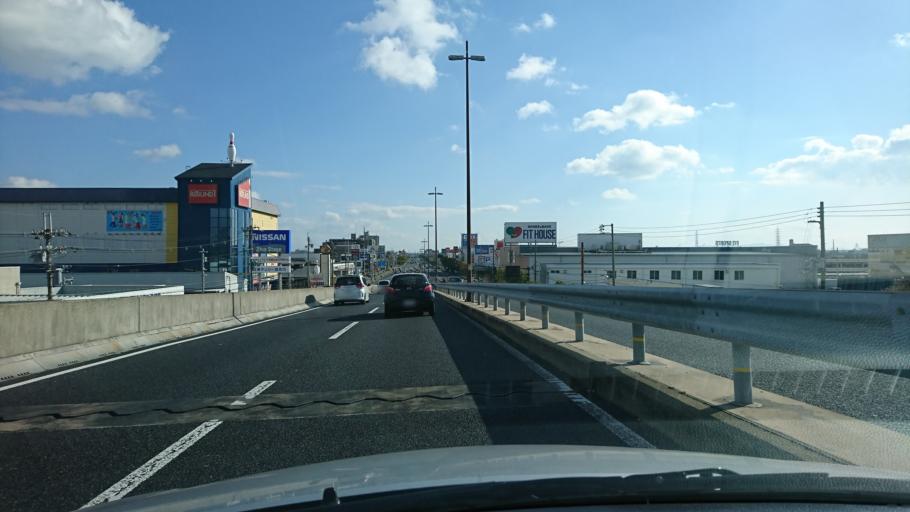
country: JP
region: Hyogo
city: Kakogawacho-honmachi
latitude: 34.7474
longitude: 134.8356
